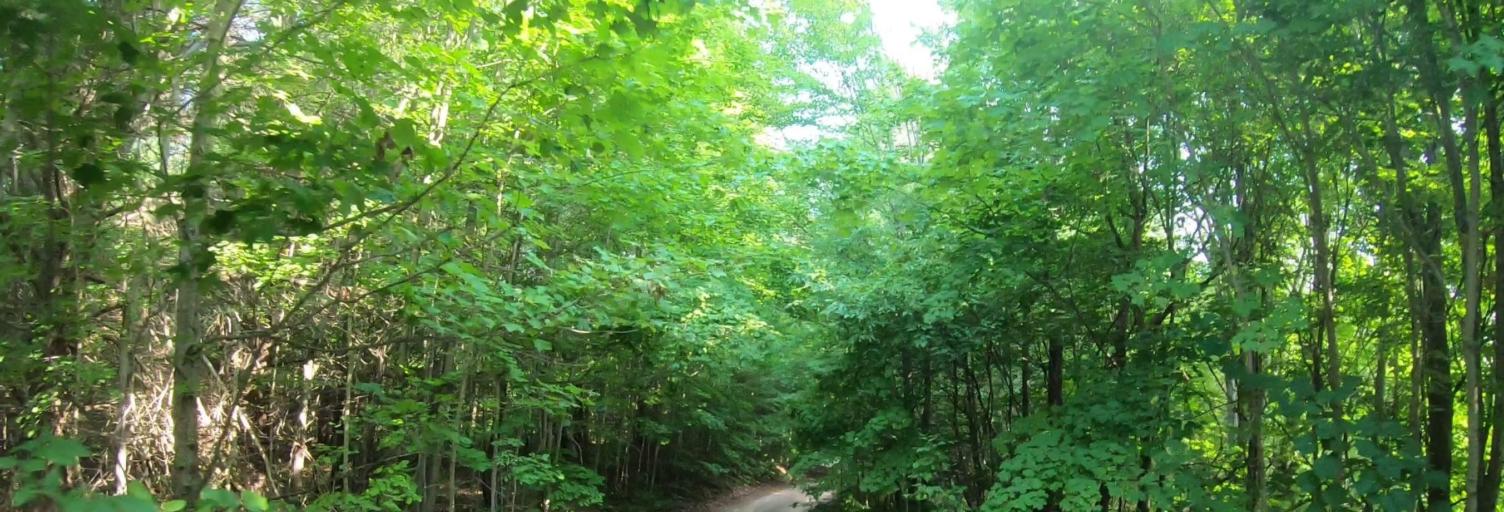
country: US
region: Michigan
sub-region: Benzie County
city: Beulah
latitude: 44.7649
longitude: -85.9293
